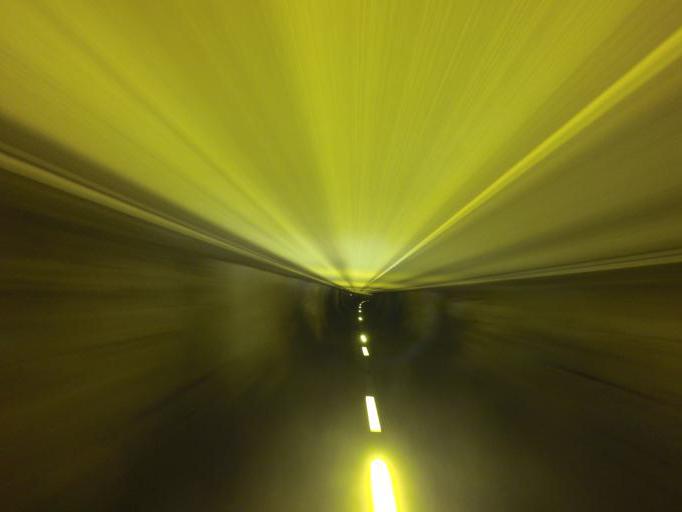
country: FO
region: Eysturoy
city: Eystur
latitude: 62.2065
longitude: -6.6789
